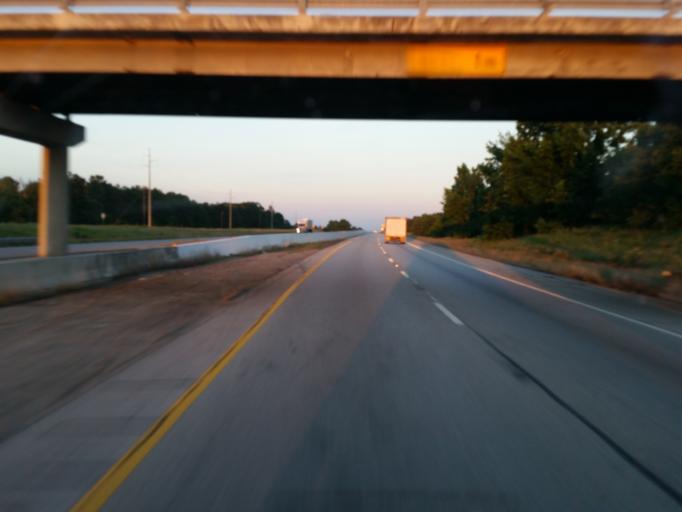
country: US
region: Texas
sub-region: Smith County
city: Hideaway
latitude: 32.4791
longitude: -95.4880
